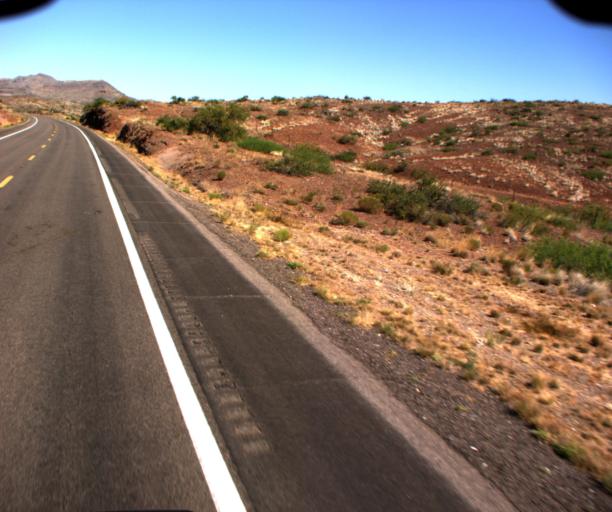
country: US
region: Arizona
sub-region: Greenlee County
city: Clifton
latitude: 32.7645
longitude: -109.2514
